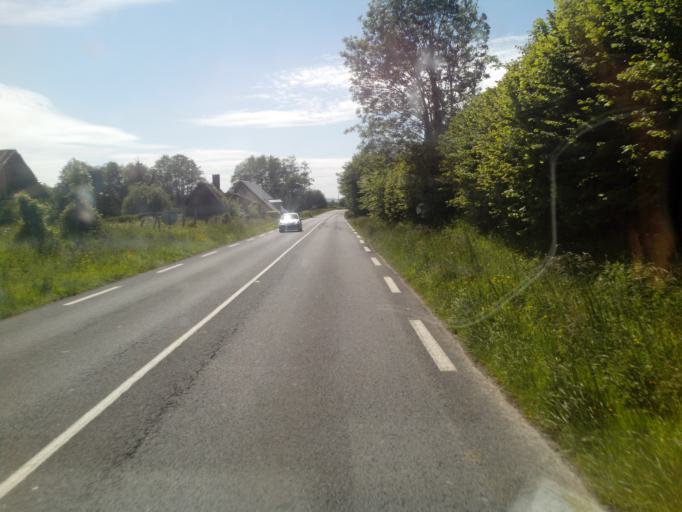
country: FR
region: Lower Normandy
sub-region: Departement du Calvados
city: Saint-Gatien-des-Bois
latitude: 49.3037
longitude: 0.2517
